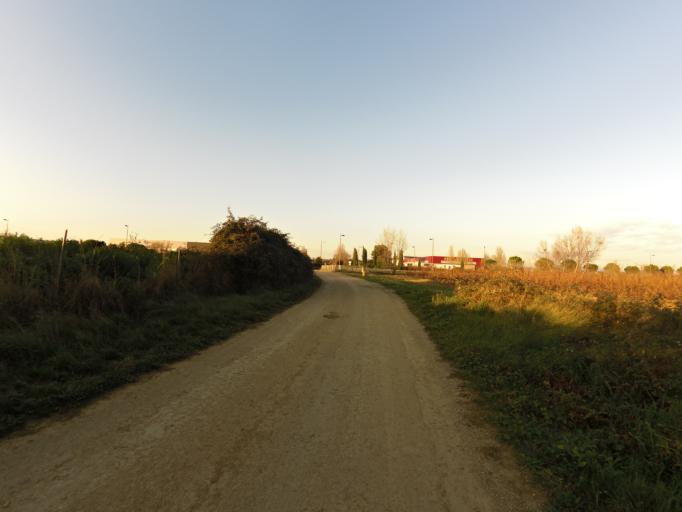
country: FR
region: Languedoc-Roussillon
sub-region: Departement du Gard
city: Aigues-Vives
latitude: 43.7181
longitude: 4.1883
